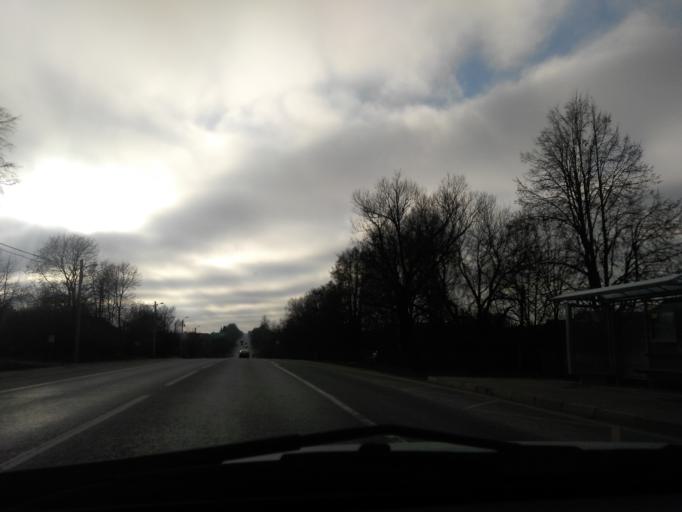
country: RU
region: Moskovskaya
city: Troitsk
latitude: 55.3054
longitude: 37.1434
